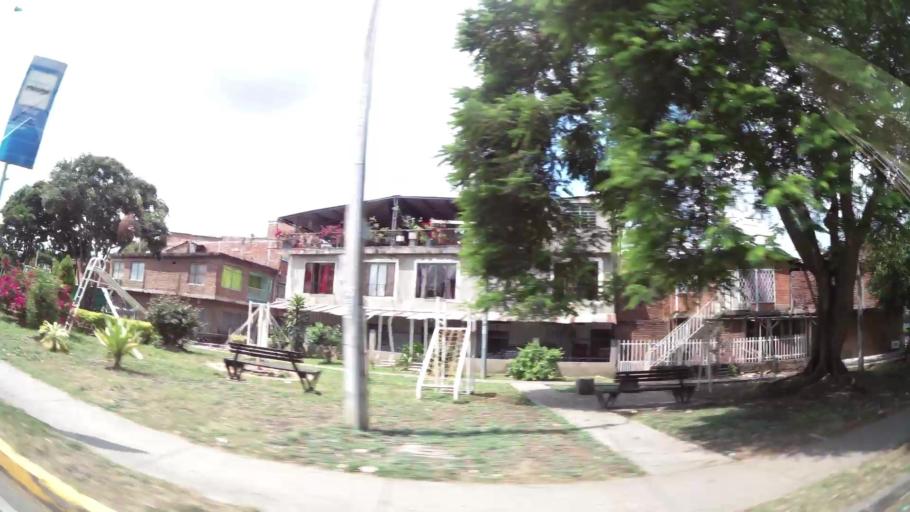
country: CO
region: Valle del Cauca
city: Cali
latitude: 3.4913
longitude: -76.4860
